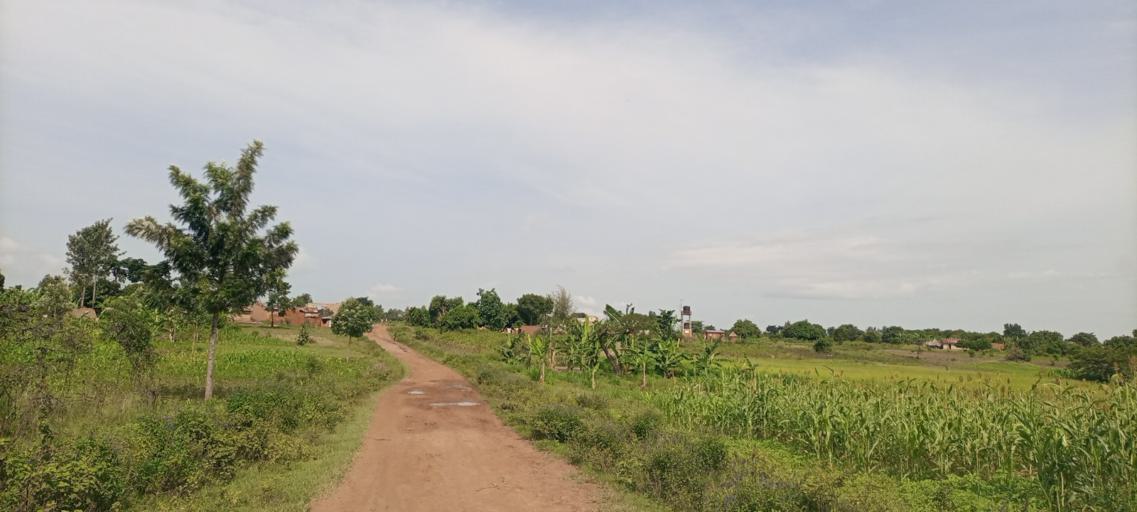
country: UG
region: Eastern Region
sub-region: Mbale District
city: Mbale
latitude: 1.1315
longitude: 34.0473
